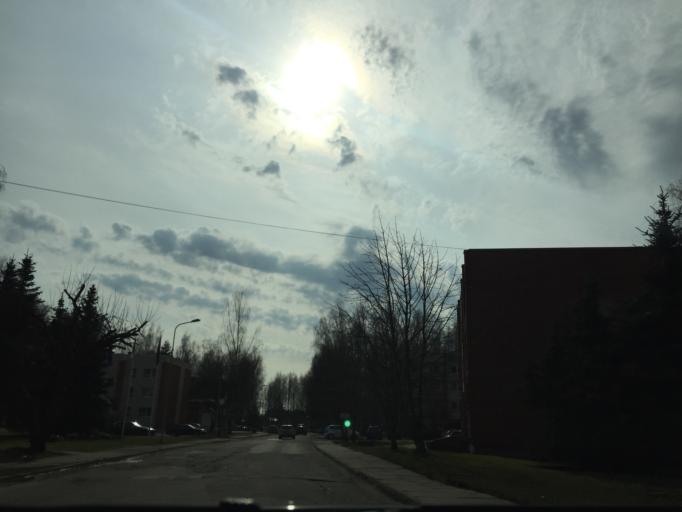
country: LV
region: Kekava
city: Balozi
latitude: 56.8814
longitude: 24.1491
